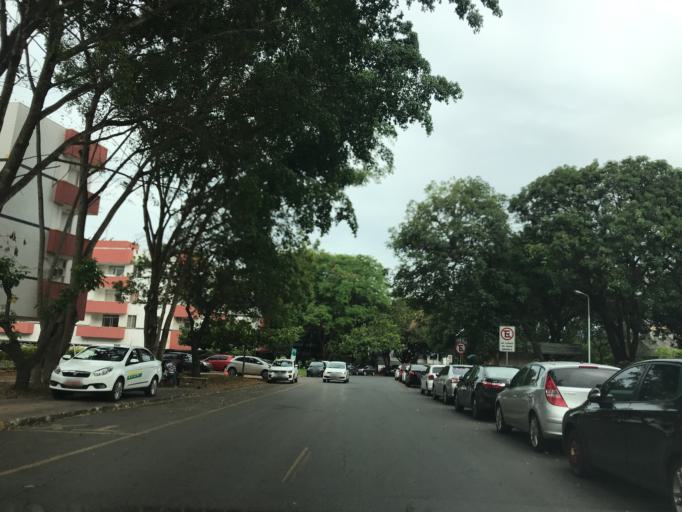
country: BR
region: Federal District
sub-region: Brasilia
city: Brasilia
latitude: -15.8060
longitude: -47.8845
